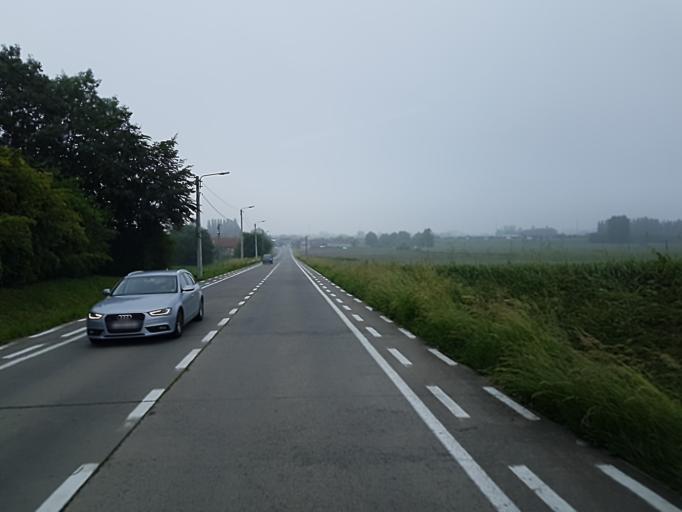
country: BE
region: Wallonia
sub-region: Province du Hainaut
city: Mouscron
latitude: 50.7638
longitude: 3.1885
